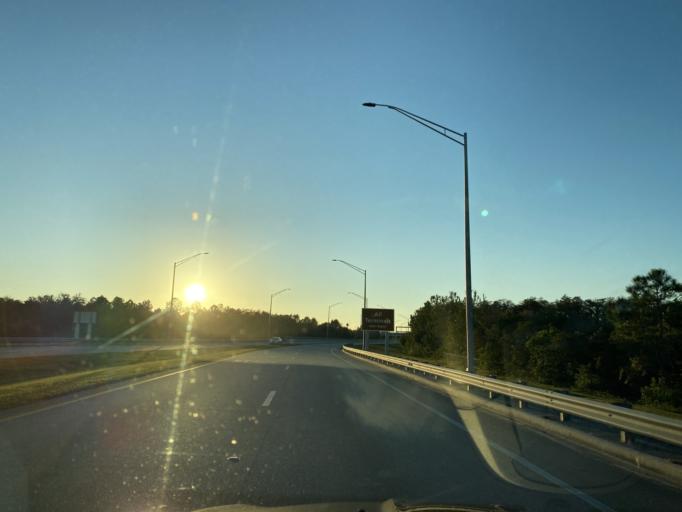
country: US
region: Florida
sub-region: Orange County
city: Meadow Woods
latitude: 28.3978
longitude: -81.3041
